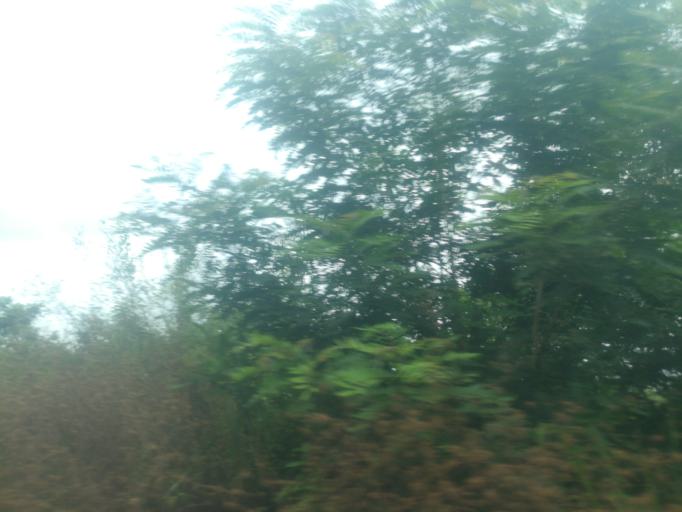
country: NG
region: Ogun
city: Itori
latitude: 7.0991
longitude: 3.1631
